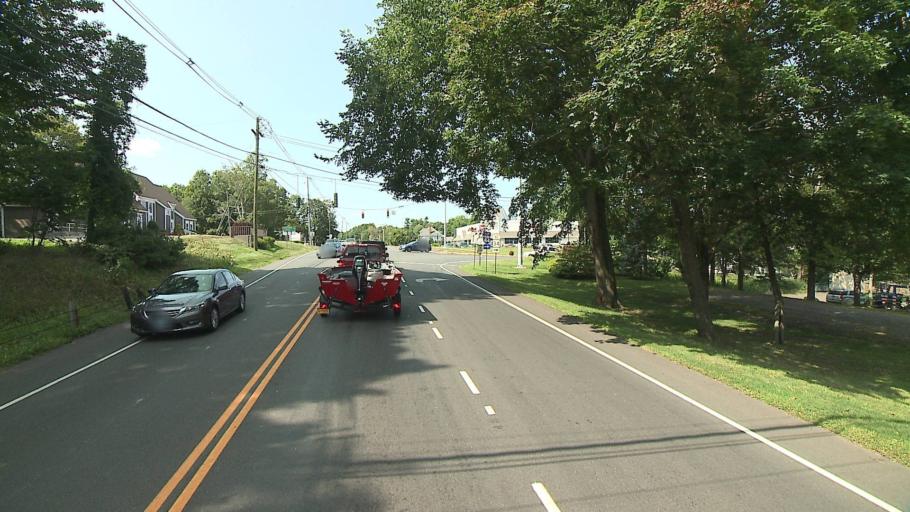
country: US
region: Connecticut
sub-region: Fairfield County
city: Newtown
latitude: 41.4008
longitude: -73.2963
